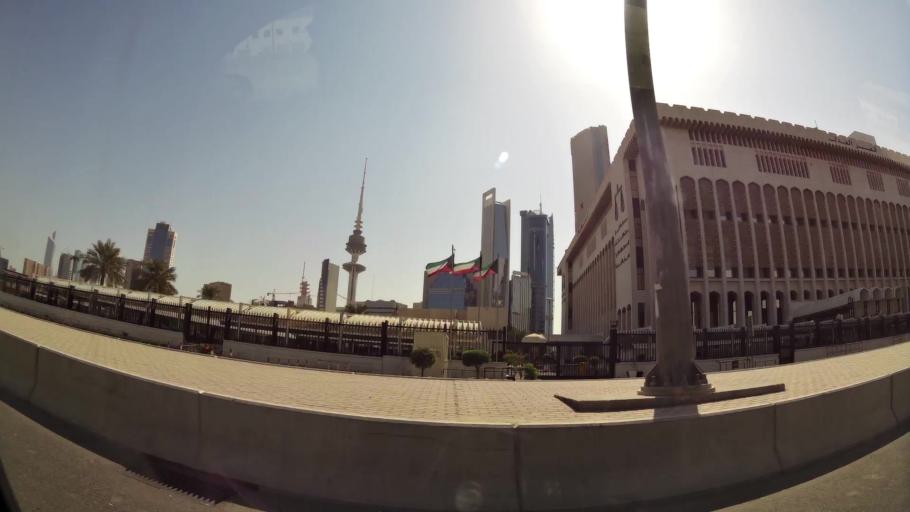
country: KW
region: Al Asimah
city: Kuwait City
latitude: 29.3706
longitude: 47.9665
